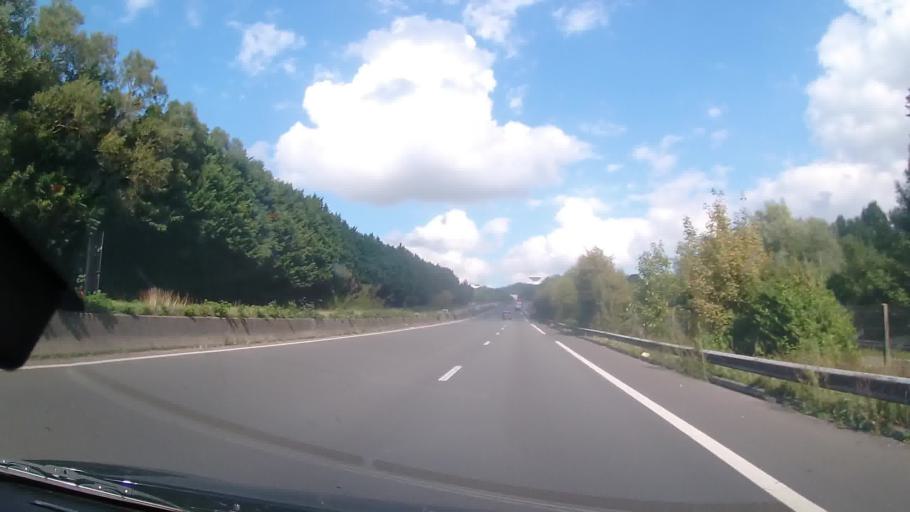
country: FR
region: Nord-Pas-de-Calais
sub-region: Departement du Pas-de-Calais
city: Wimille
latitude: 50.7627
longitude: 1.6362
